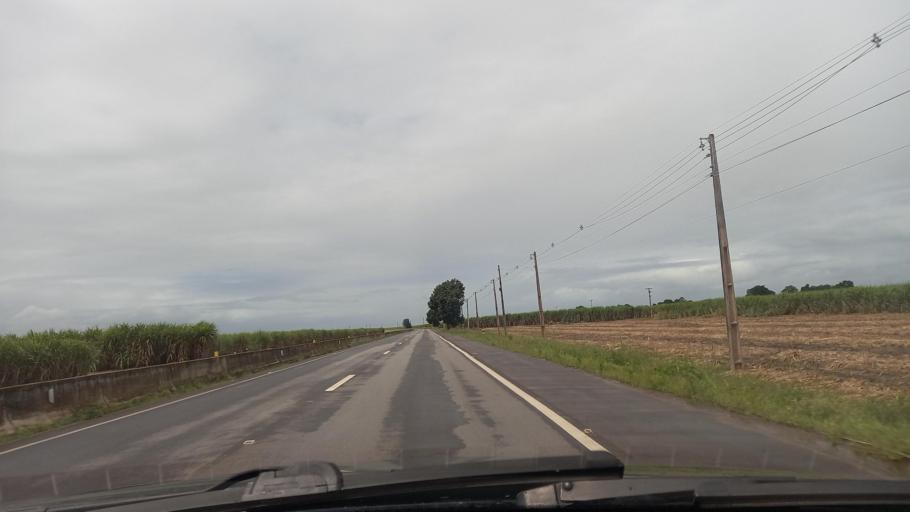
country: BR
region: Alagoas
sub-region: Campo Alegre
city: Campo Alegre
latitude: -9.8198
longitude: -36.2465
